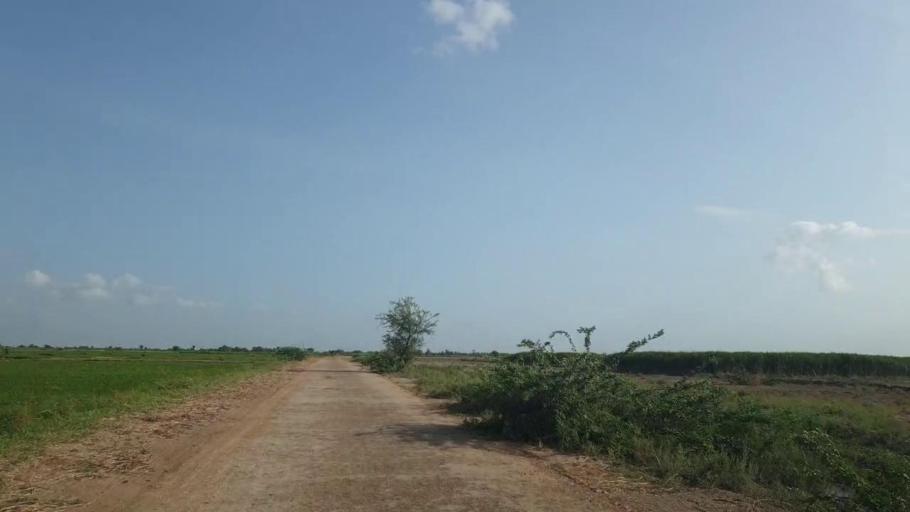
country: PK
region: Sindh
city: Kadhan
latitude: 24.6131
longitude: 69.0919
